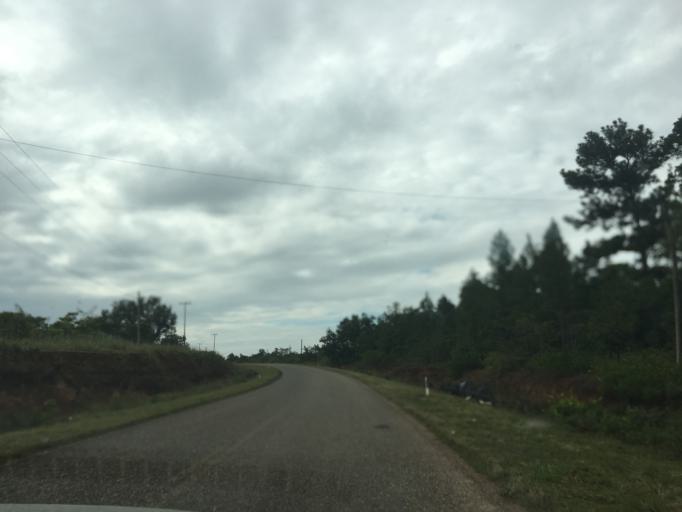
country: BZ
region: Stann Creek
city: Placencia
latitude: 16.7618
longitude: -88.3854
